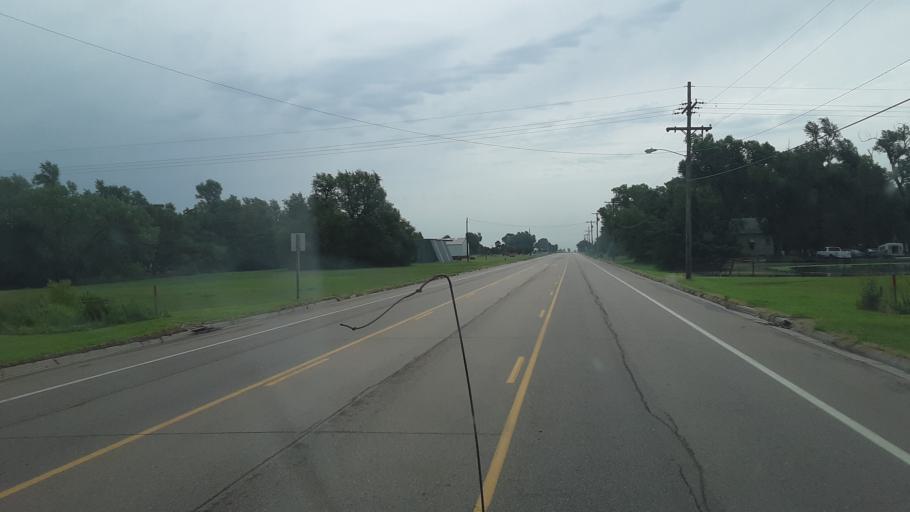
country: US
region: Kansas
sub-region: Stafford County
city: Saint John
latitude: 37.9566
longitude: -98.9642
